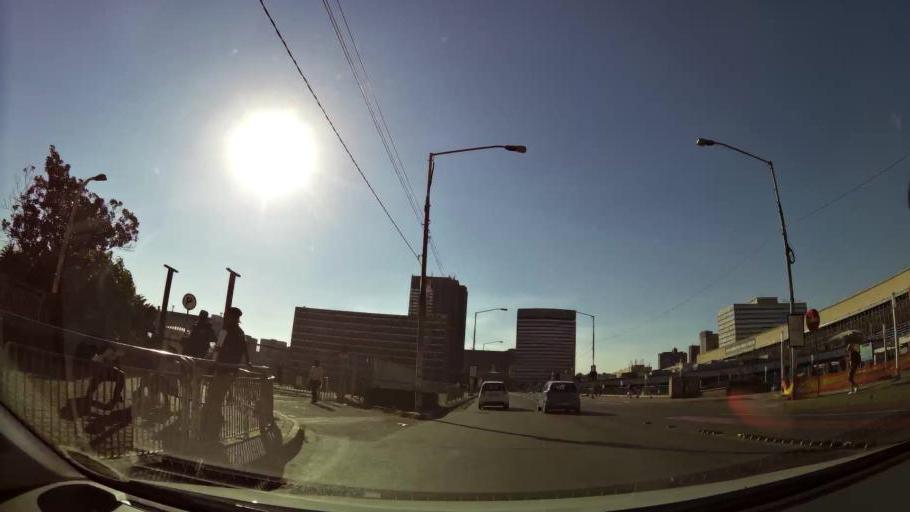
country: ZA
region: Gauteng
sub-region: City of Johannesburg Metropolitan Municipality
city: Johannesburg
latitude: -26.1986
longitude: 28.0413
